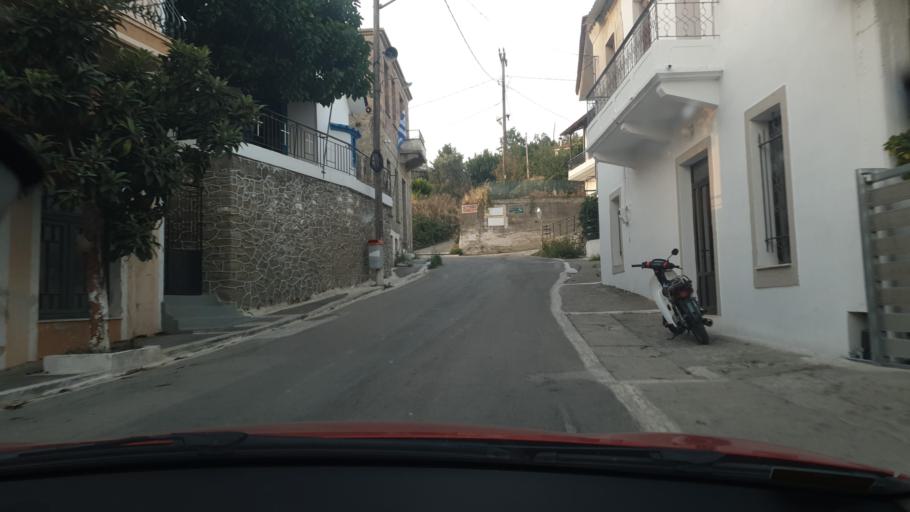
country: GR
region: Central Greece
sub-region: Nomos Evvoias
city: Oxilithos
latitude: 38.5807
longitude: 24.1119
